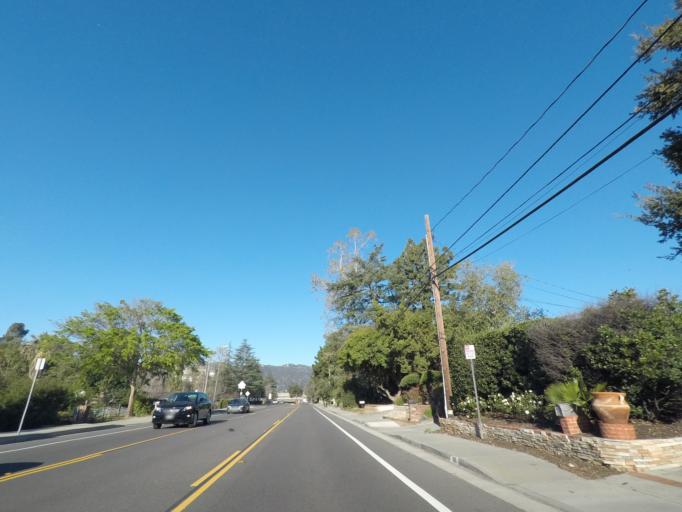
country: US
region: California
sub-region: Los Angeles County
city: La Canada Flintridge
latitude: 34.2057
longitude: -118.2123
